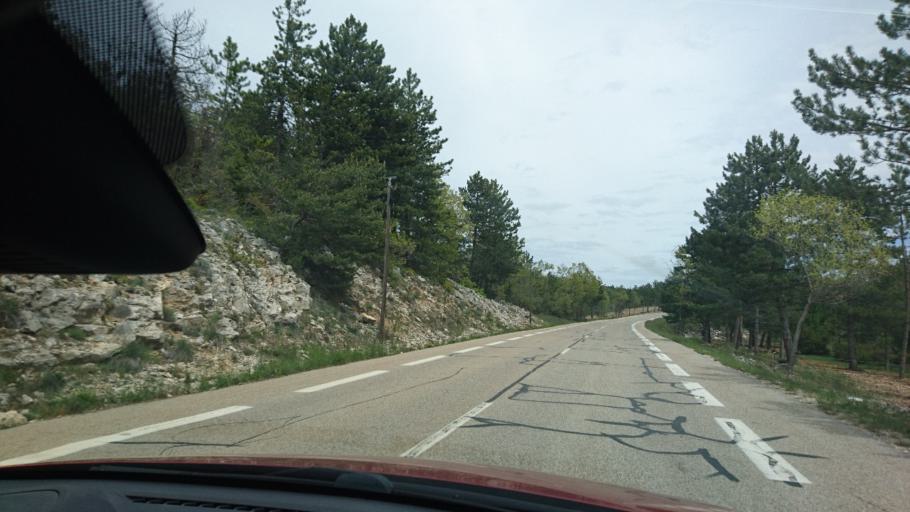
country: FR
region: Provence-Alpes-Cote d'Azur
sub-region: Departement du Vaucluse
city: Villes-sur-Auzon
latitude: 44.0933
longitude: 5.3172
